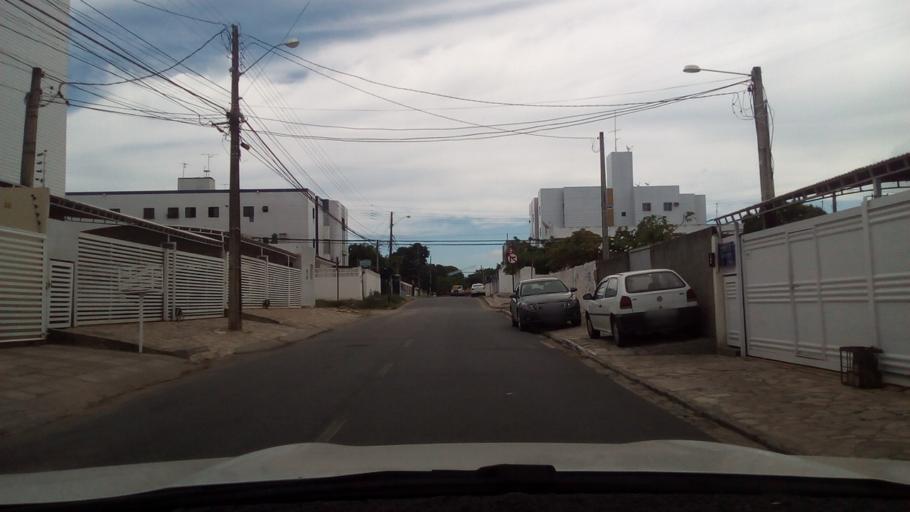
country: BR
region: Paraiba
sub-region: Joao Pessoa
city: Joao Pessoa
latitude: -7.1577
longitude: -34.8345
